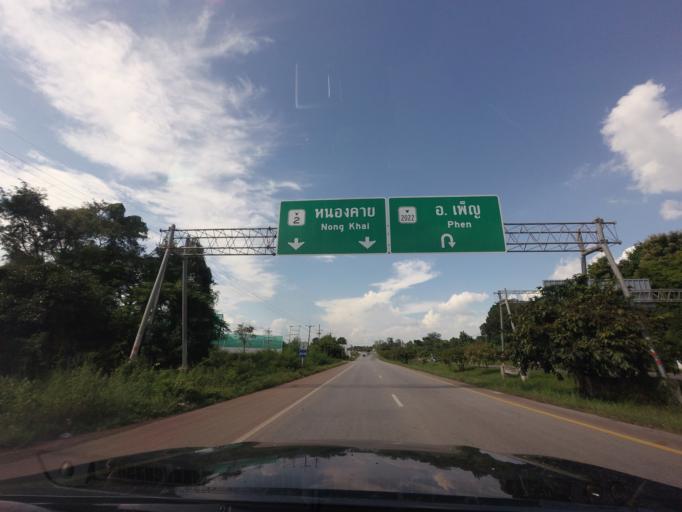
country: TH
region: Nong Khai
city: Sa Khrai
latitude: 17.6674
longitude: 102.7906
